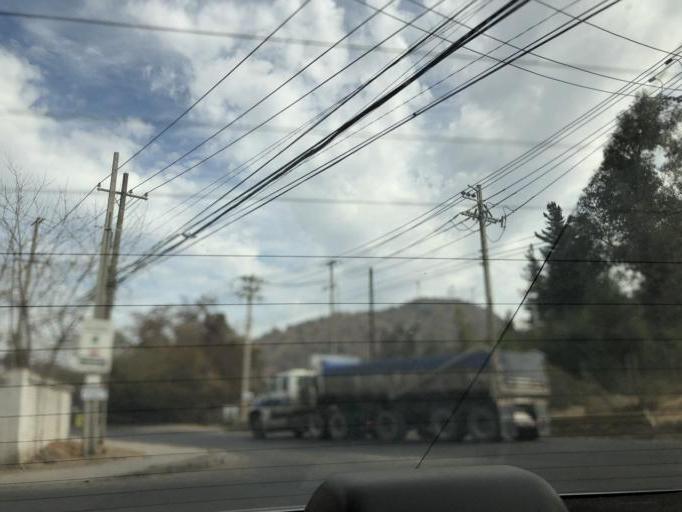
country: CL
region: Santiago Metropolitan
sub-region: Provincia de Cordillera
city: Puente Alto
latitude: -33.6075
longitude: -70.5368
